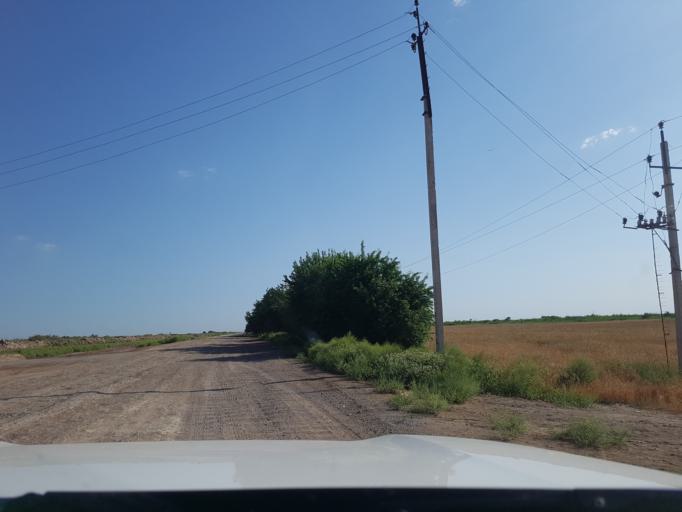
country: TM
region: Dasoguz
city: Koeneuergench
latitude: 41.9343
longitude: 58.7143
